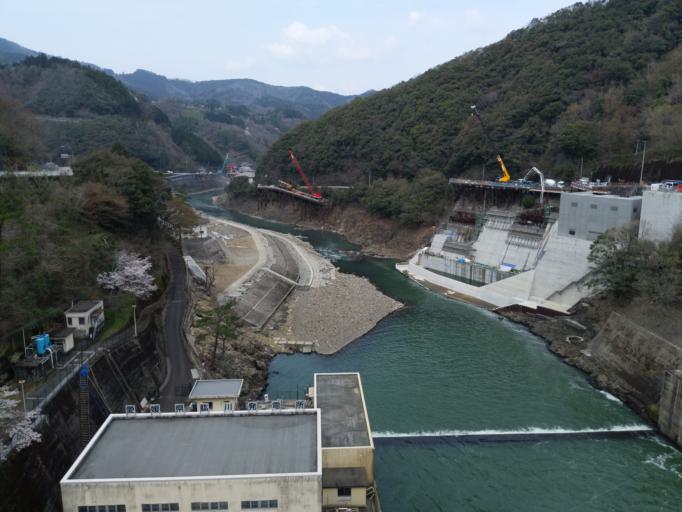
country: JP
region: Ehime
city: Ozu
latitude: 33.4501
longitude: 132.6851
